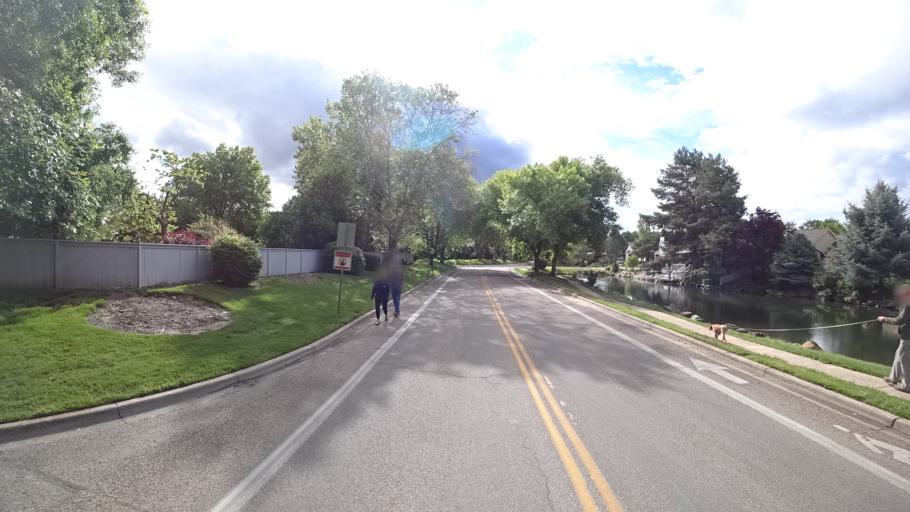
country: US
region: Idaho
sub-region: Ada County
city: Garden City
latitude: 43.6652
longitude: -116.2897
